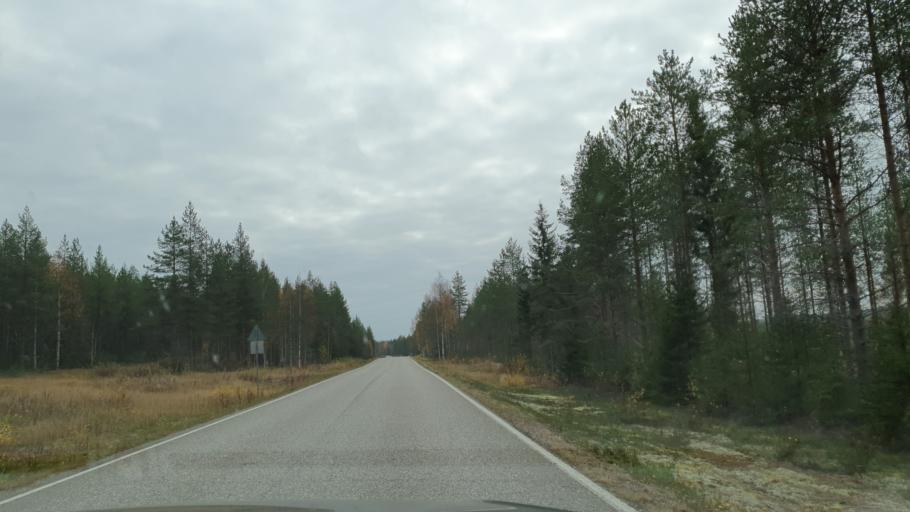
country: FI
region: Kainuu
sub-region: Kajaani
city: Ristijaervi
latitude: 64.6224
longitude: 27.9947
